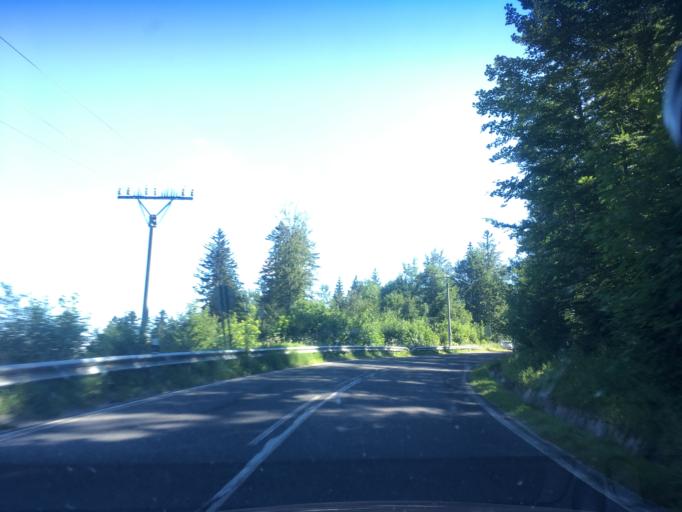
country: PL
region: Lesser Poland Voivodeship
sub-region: Powiat tatrzanski
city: Bukowina Tatrzanska
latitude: 49.2677
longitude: 20.1259
